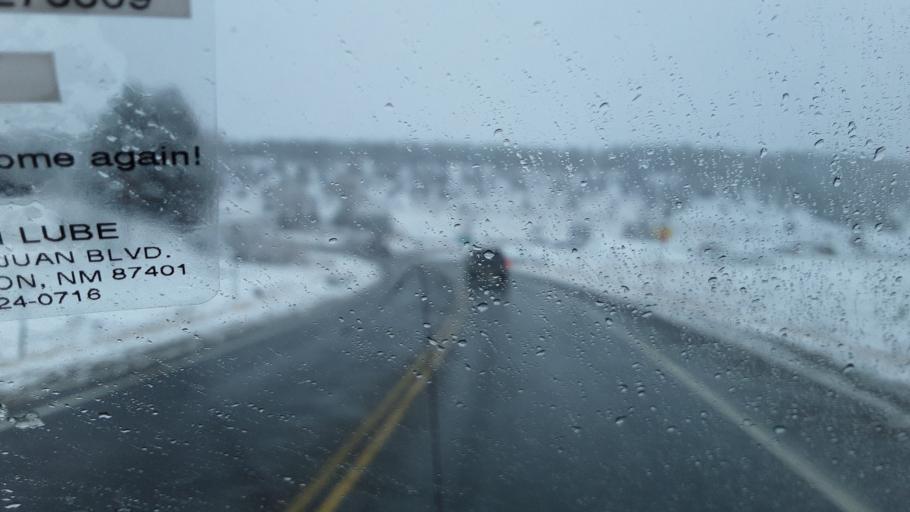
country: US
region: Colorado
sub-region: Archuleta County
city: Pagosa Springs
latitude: 37.2688
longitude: -106.9963
